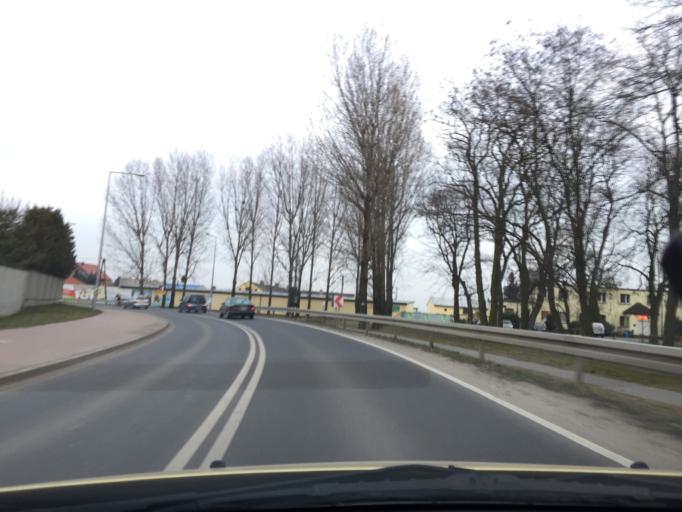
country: PL
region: Greater Poland Voivodeship
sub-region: Powiat poznanski
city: Plewiska
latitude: 52.3880
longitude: 16.7846
